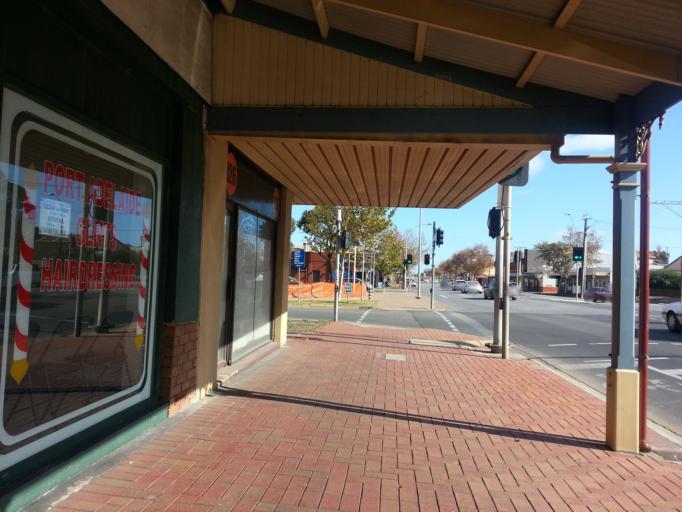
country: AU
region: South Australia
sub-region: Port Adelaide Enfield
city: Birkenhead
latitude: -34.8449
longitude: 138.5029
